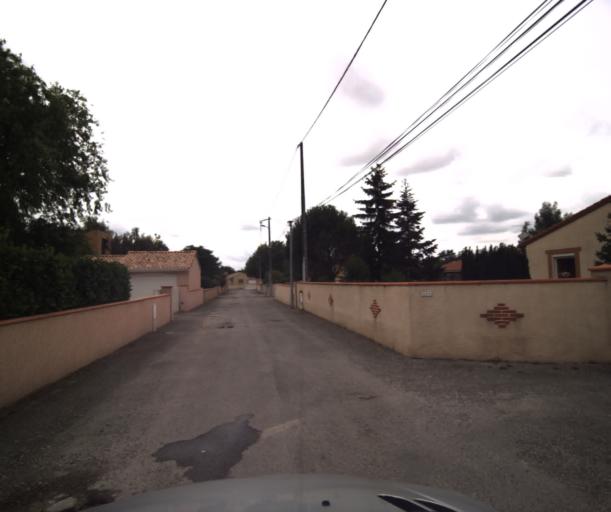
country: FR
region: Midi-Pyrenees
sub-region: Departement de la Haute-Garonne
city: Labarthe-sur-Leze
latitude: 43.4559
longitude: 1.4013
